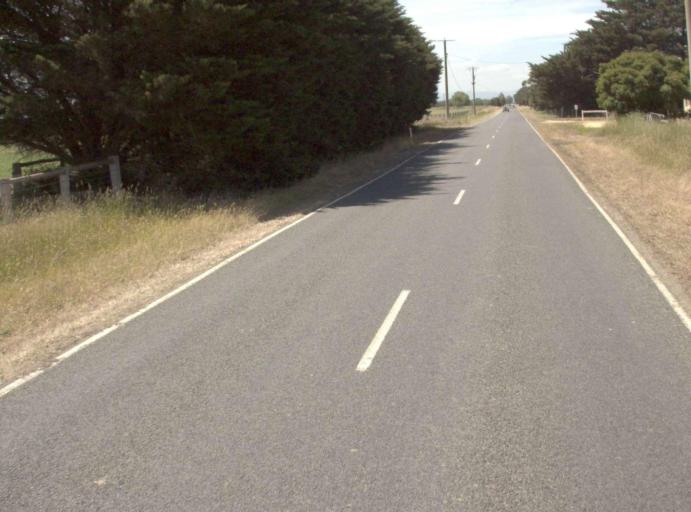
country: AU
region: Victoria
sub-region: Wellington
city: Heyfield
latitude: -38.0654
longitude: 146.8718
